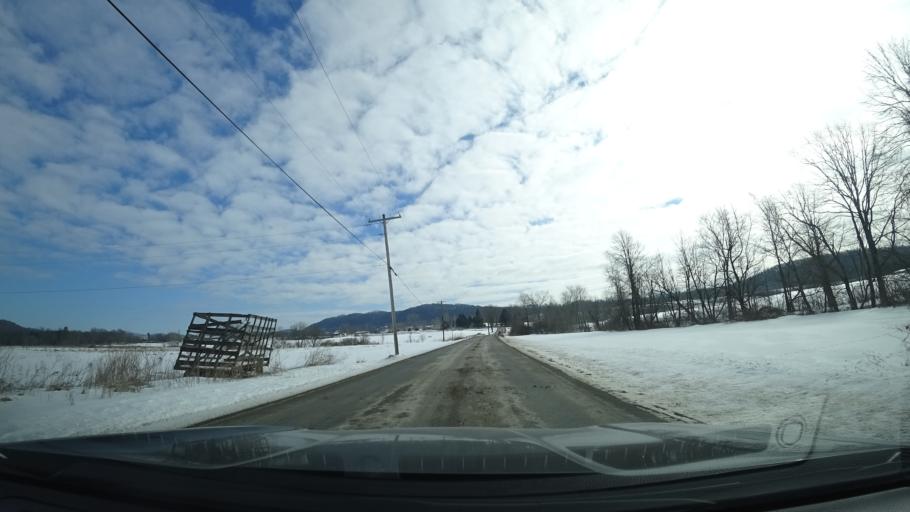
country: US
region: New York
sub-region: Washington County
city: Fort Edward
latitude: 43.2536
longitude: -73.4784
